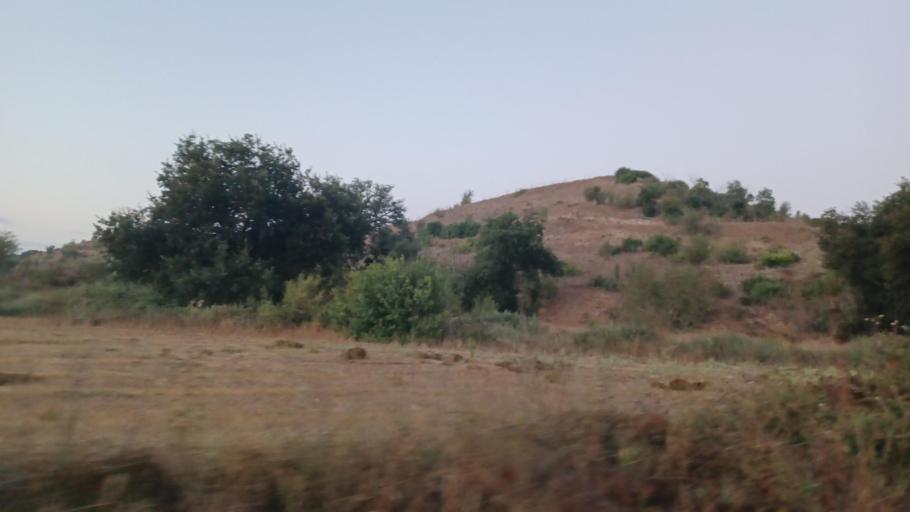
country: CY
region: Pafos
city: Mesogi
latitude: 34.8553
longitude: 32.5418
